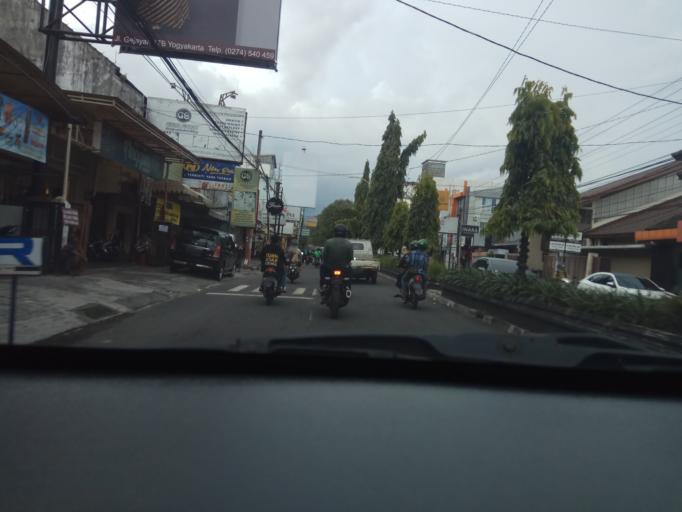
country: ID
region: Daerah Istimewa Yogyakarta
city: Yogyakarta
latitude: -7.7689
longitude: 110.3910
